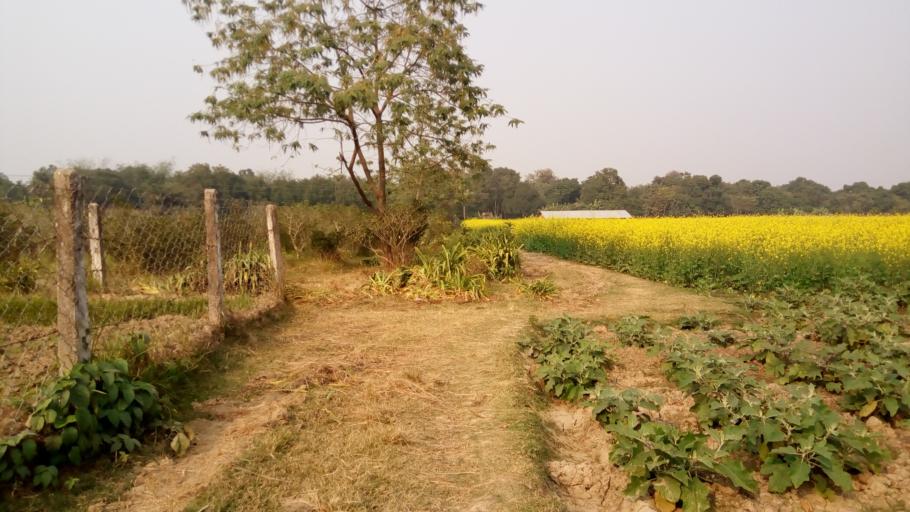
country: IN
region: West Bengal
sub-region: Nadia
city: Navadwip
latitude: 23.4452
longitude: 88.4175
